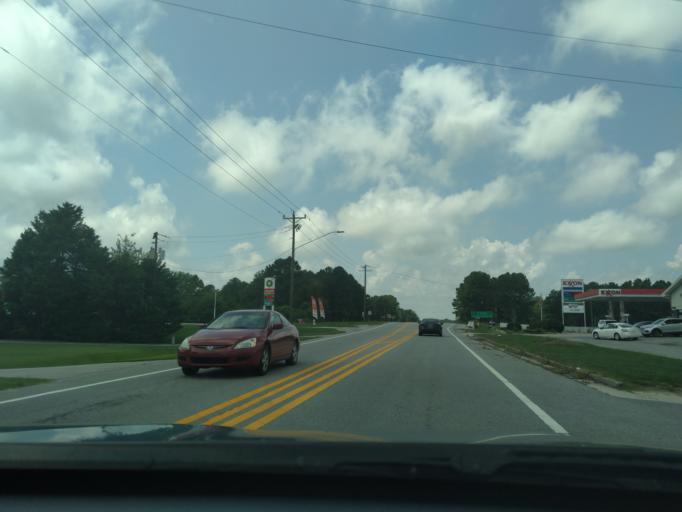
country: US
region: North Carolina
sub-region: Nash County
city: Red Oak
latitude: 36.0125
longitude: -77.8596
